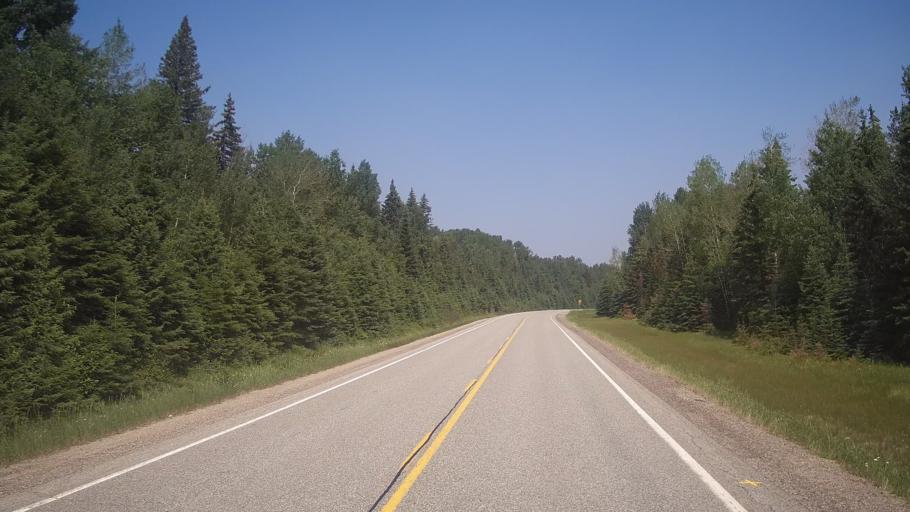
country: CA
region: Ontario
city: Timmins
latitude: 48.2288
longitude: -81.5757
